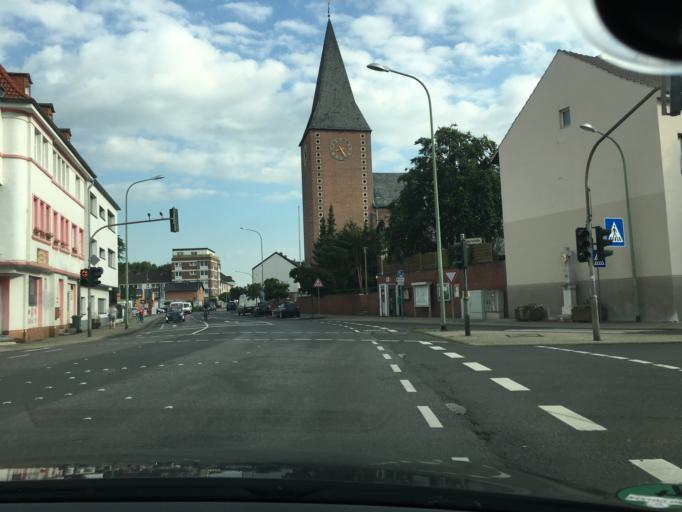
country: DE
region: North Rhine-Westphalia
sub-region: Regierungsbezirk Koln
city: Dueren
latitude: 50.8228
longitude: 6.4612
